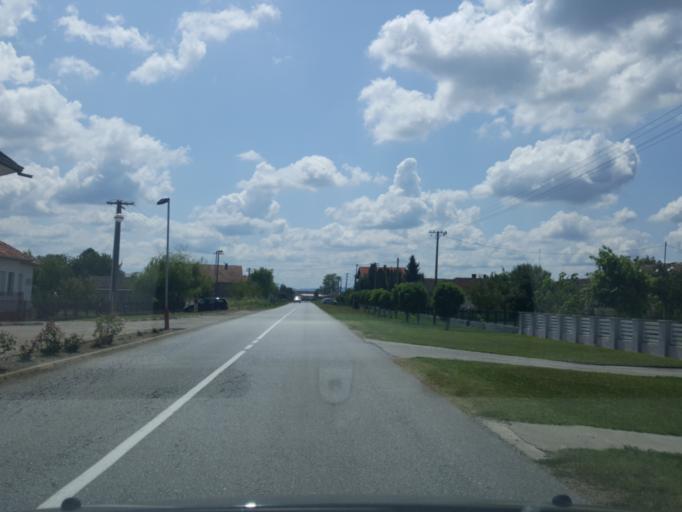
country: RS
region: Central Serbia
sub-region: Macvanski Okrug
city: Bogatic
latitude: 44.8251
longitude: 19.4778
